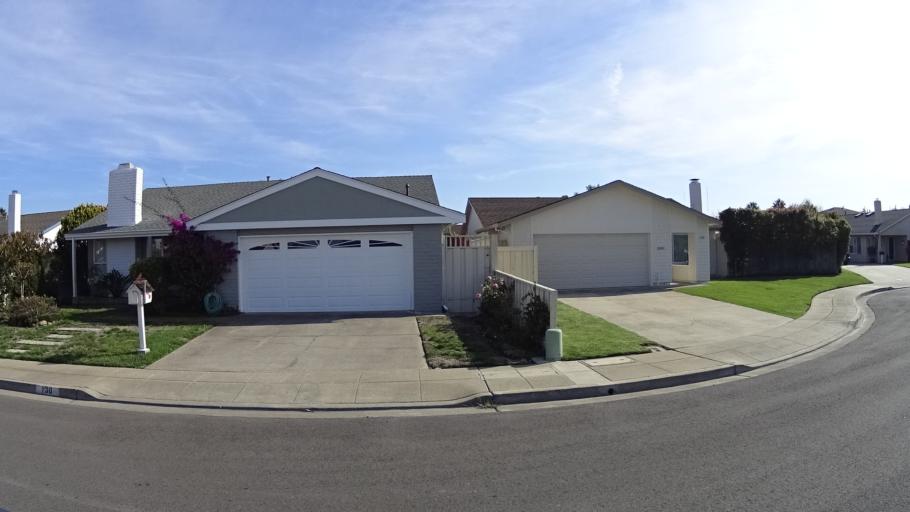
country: US
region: California
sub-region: San Mateo County
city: Belmont
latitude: 37.5369
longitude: -122.2770
